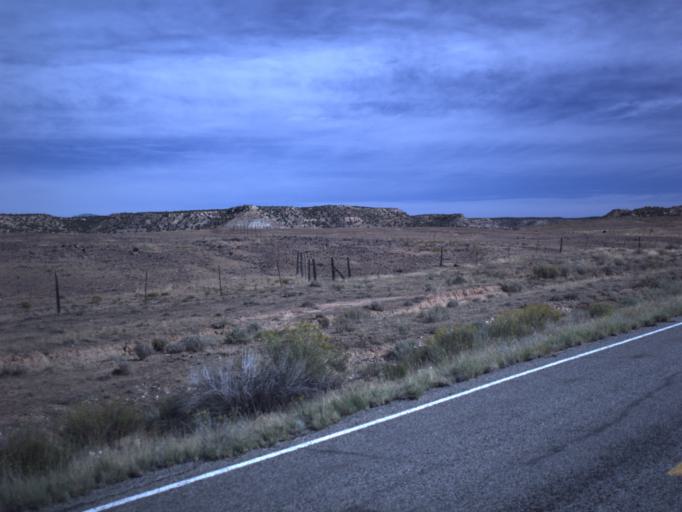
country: US
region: Utah
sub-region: San Juan County
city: Blanding
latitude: 37.4268
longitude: -109.4127
